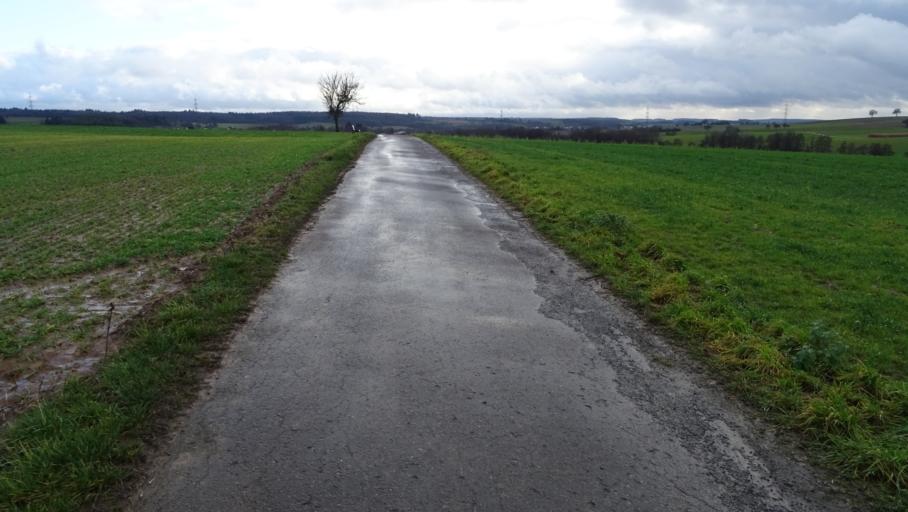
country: DE
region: Baden-Wuerttemberg
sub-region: Karlsruhe Region
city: Seckach
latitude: 49.4396
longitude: 9.2804
